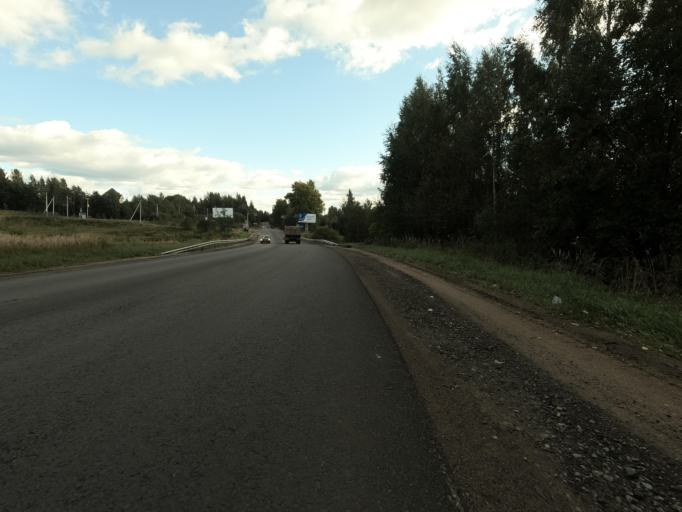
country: RU
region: Leningrad
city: Koltushi
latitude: 59.9712
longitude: 30.6531
